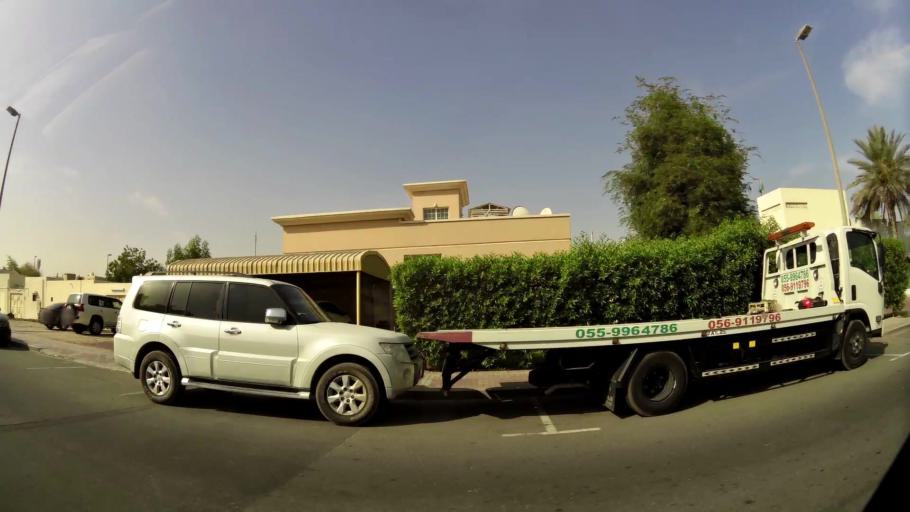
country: AE
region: Ash Shariqah
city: Sharjah
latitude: 25.2222
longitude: 55.3855
